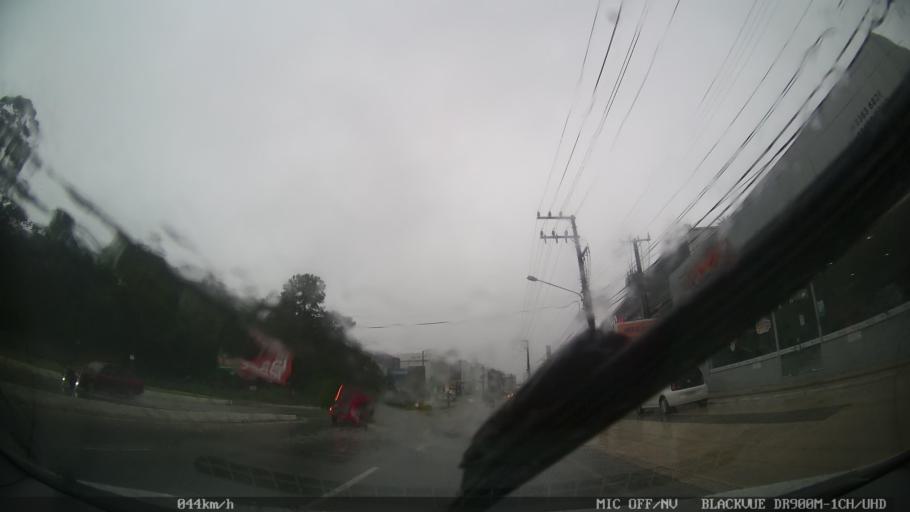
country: BR
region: Santa Catarina
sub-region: Balneario Camboriu
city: Balneario Camboriu
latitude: -26.9585
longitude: -48.6394
